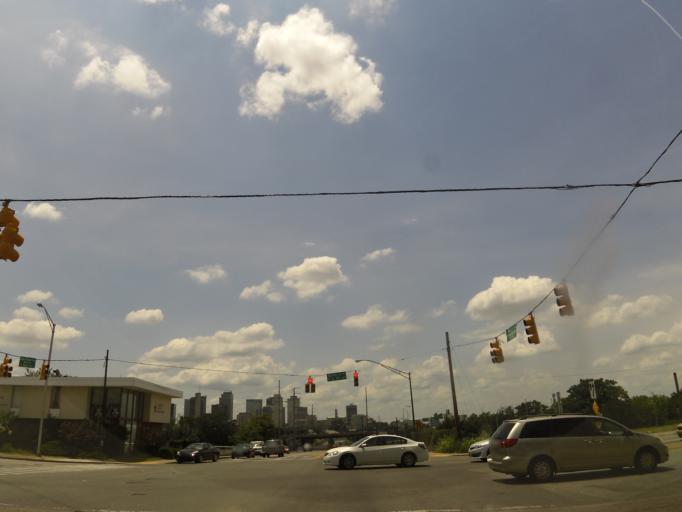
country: US
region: Tennessee
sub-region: Davidson County
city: Nashville
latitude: 36.1730
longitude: -86.7652
